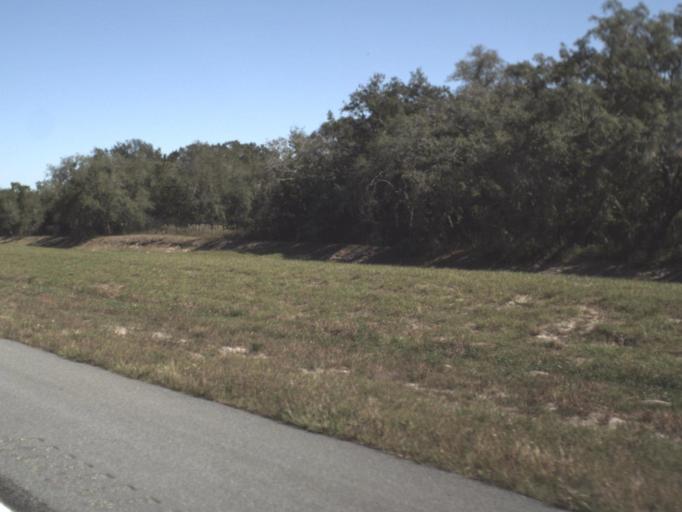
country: US
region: Florida
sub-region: Pasco County
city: Shady Hills
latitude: 28.3672
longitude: -82.5447
